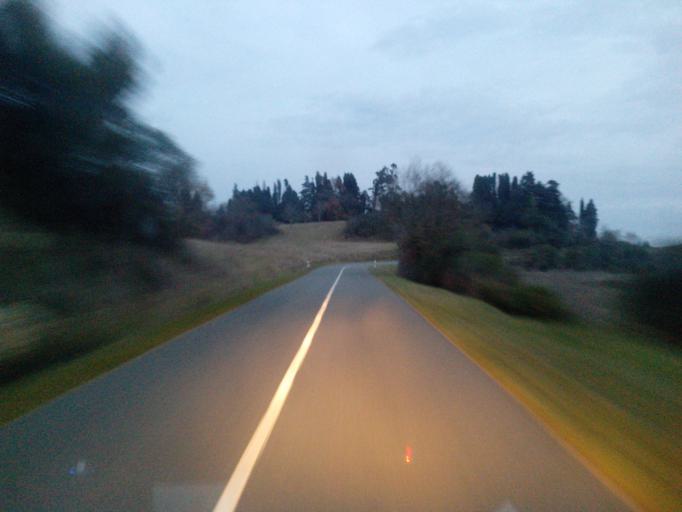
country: FR
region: Midi-Pyrenees
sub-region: Departement de la Haute-Garonne
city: Avignonet-Lauragais
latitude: 43.2764
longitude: 1.8065
